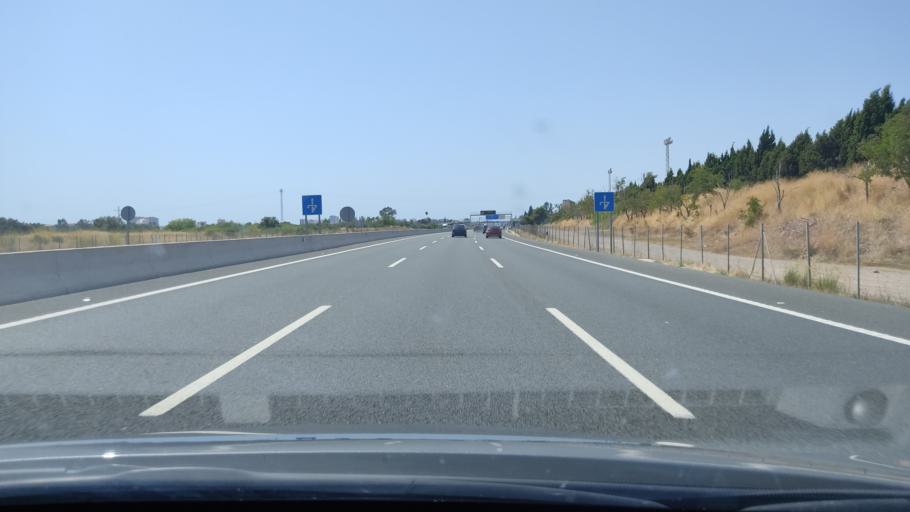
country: ES
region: Valencia
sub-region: Provincia de Valencia
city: Puig
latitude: 39.5941
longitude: -0.2932
